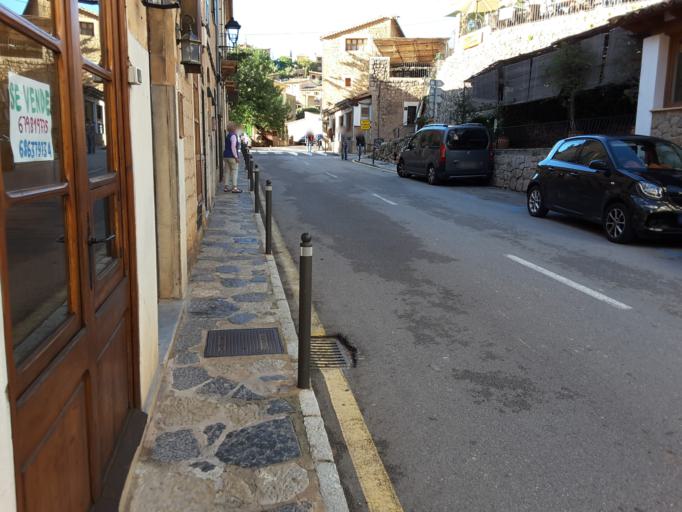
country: ES
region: Balearic Islands
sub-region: Illes Balears
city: Deia
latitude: 39.7469
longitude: 2.6492
